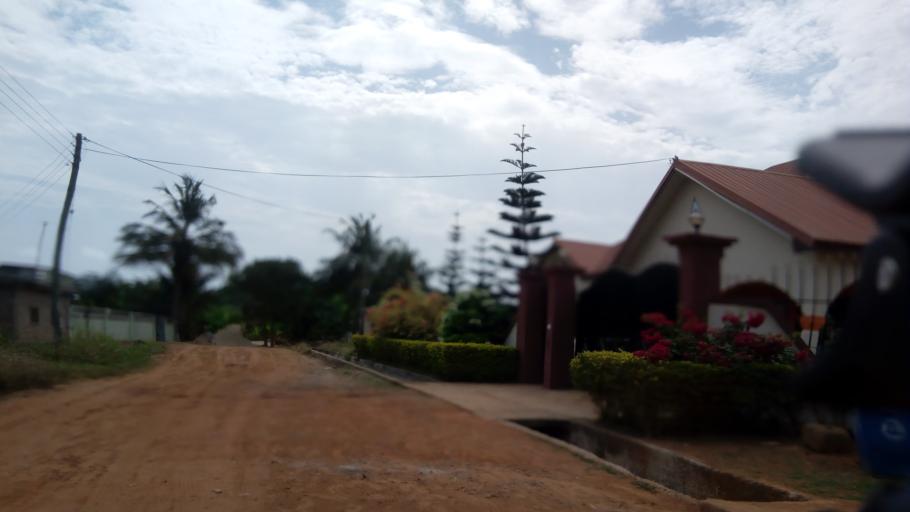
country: GH
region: Central
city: Cape Coast
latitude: 5.1078
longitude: -1.2707
